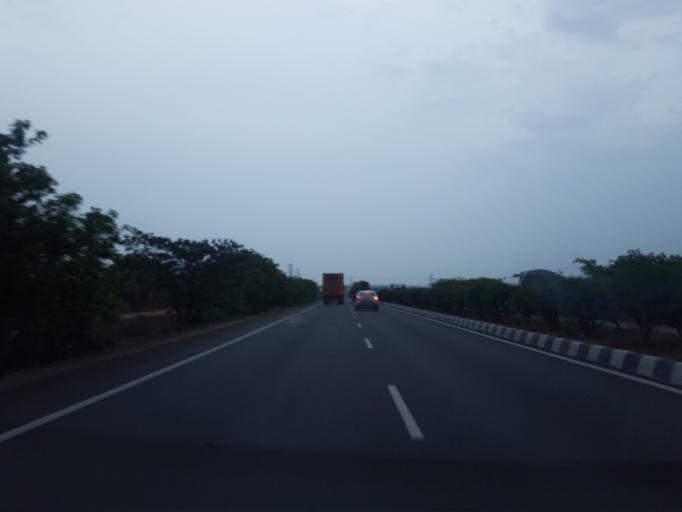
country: IN
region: Telangana
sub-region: Mahbubnagar
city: Farrukhnagar
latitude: 17.1002
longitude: 78.2508
